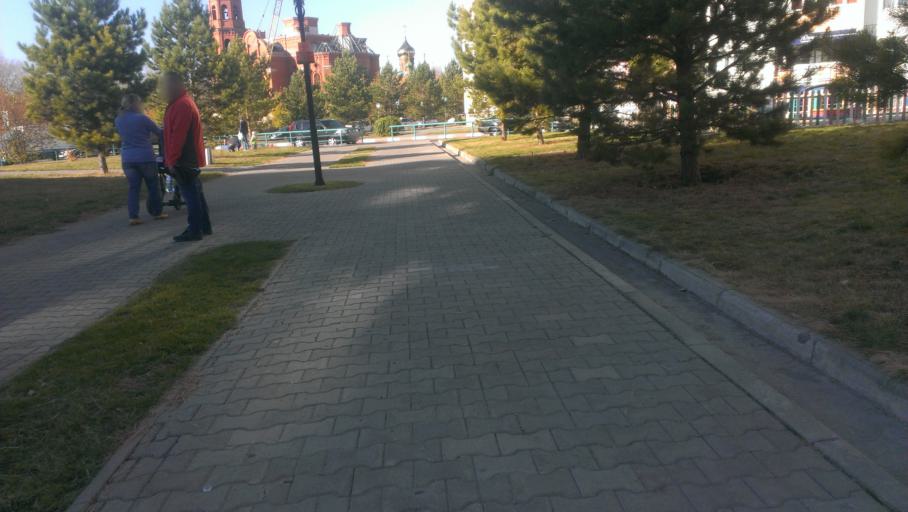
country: RU
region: Altai Krai
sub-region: Gorod Barnaulskiy
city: Barnaul
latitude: 53.3582
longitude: 83.6919
